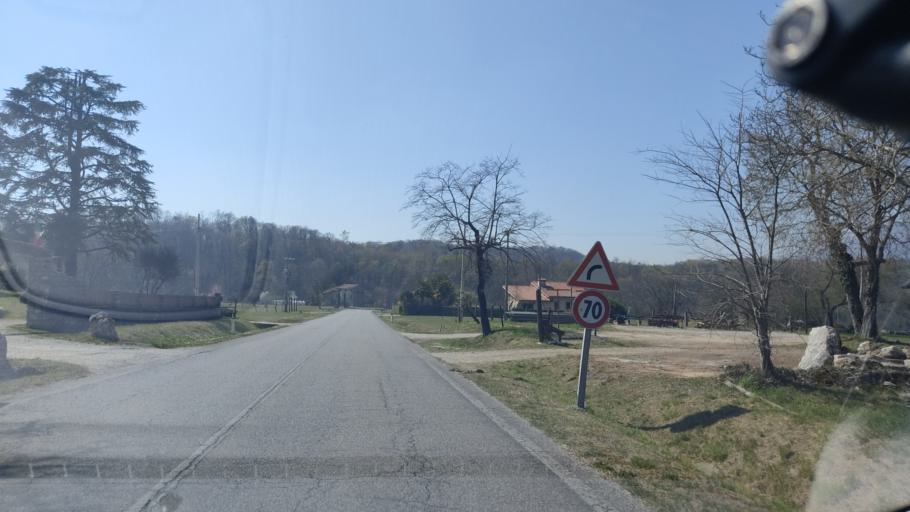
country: IT
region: Friuli Venezia Giulia
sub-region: Provincia di Pordenone
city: Budoia
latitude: 46.0450
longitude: 12.5255
